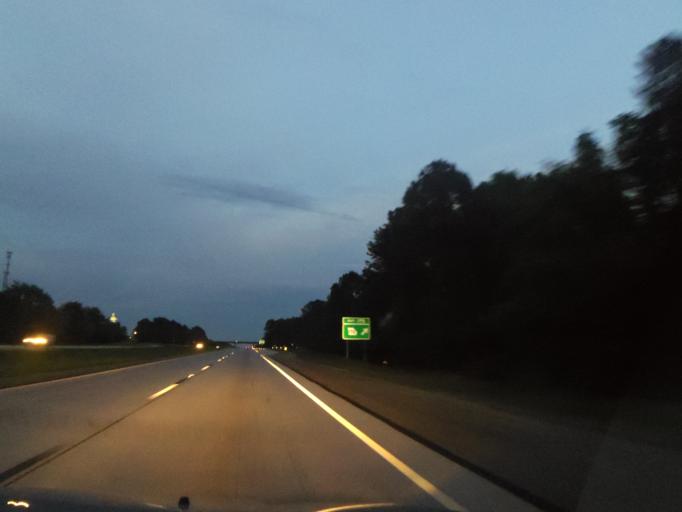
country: US
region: Georgia
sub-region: McDuffie County
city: Thomson
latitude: 33.5118
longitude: -82.4531
